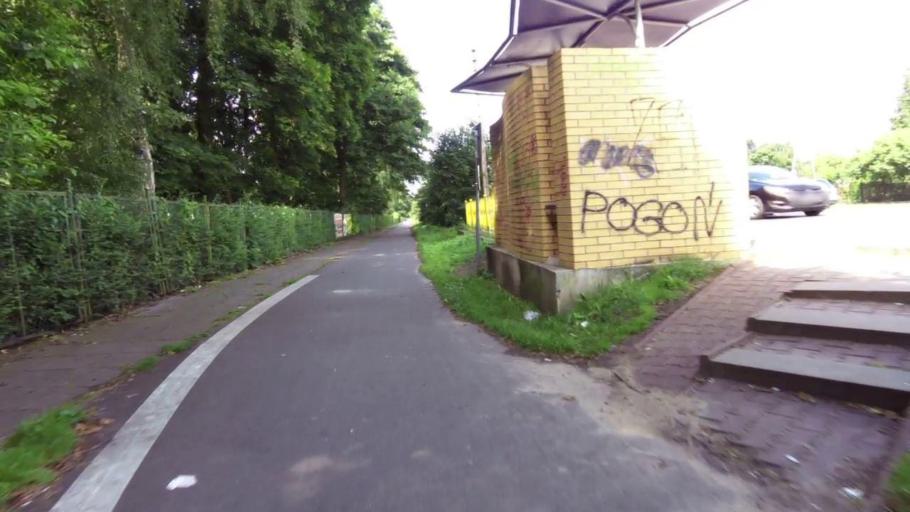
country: PL
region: West Pomeranian Voivodeship
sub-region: Powiat stargardzki
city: Kobylanka
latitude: 53.3511
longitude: 14.9309
